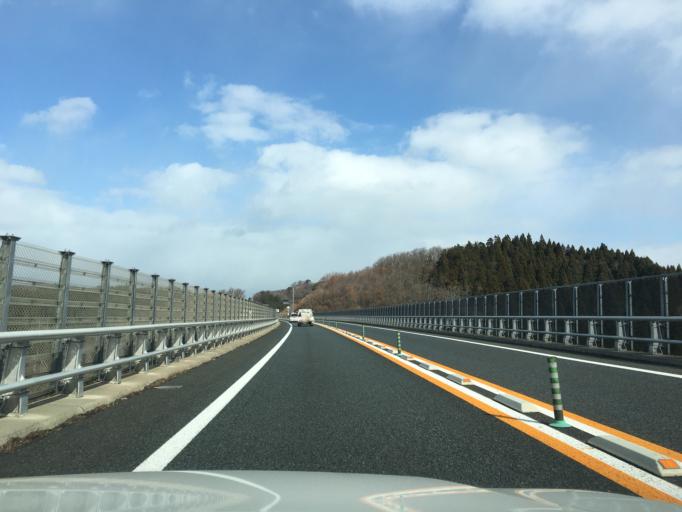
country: JP
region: Akita
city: Akita Shi
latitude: 39.4669
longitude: 140.0587
